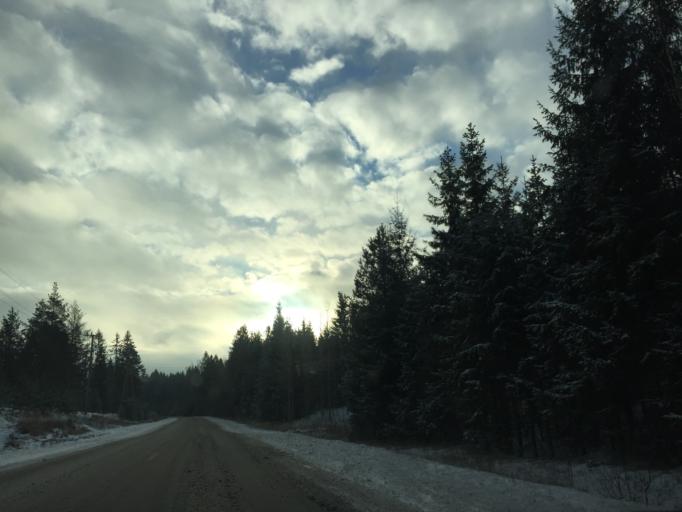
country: LV
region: Amatas Novads
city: Drabesi
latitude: 57.2236
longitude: 25.2840
